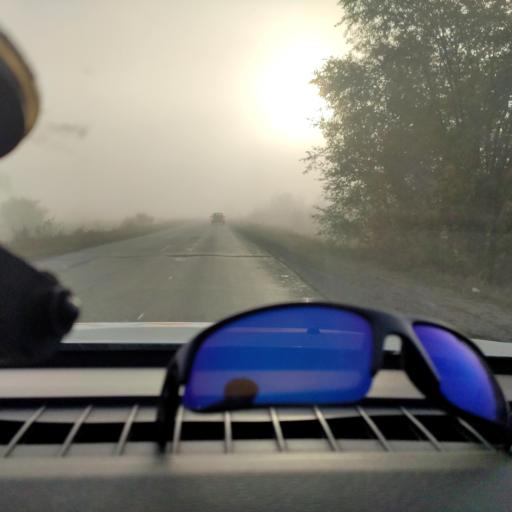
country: RU
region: Samara
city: Chapayevsk
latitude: 53.0009
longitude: 49.7602
